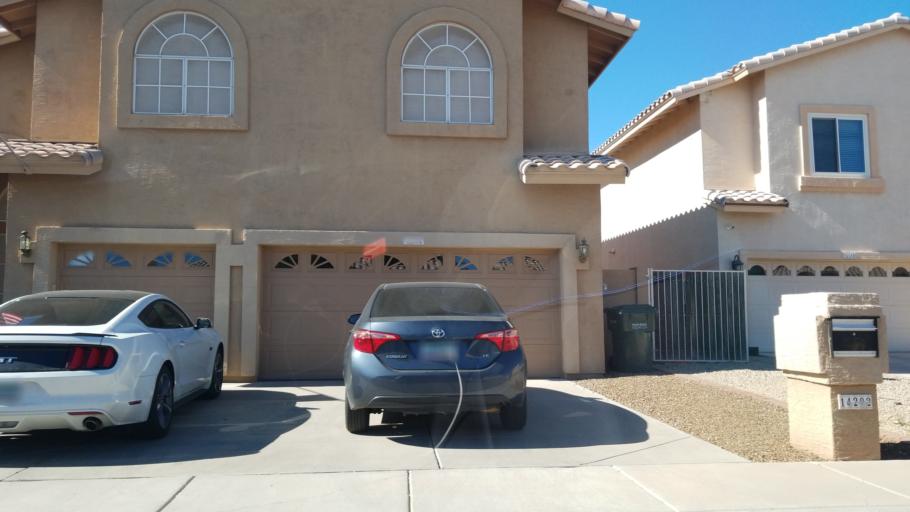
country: US
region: Arizona
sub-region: Maricopa County
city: Paradise Valley
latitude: 33.6152
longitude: -111.9335
